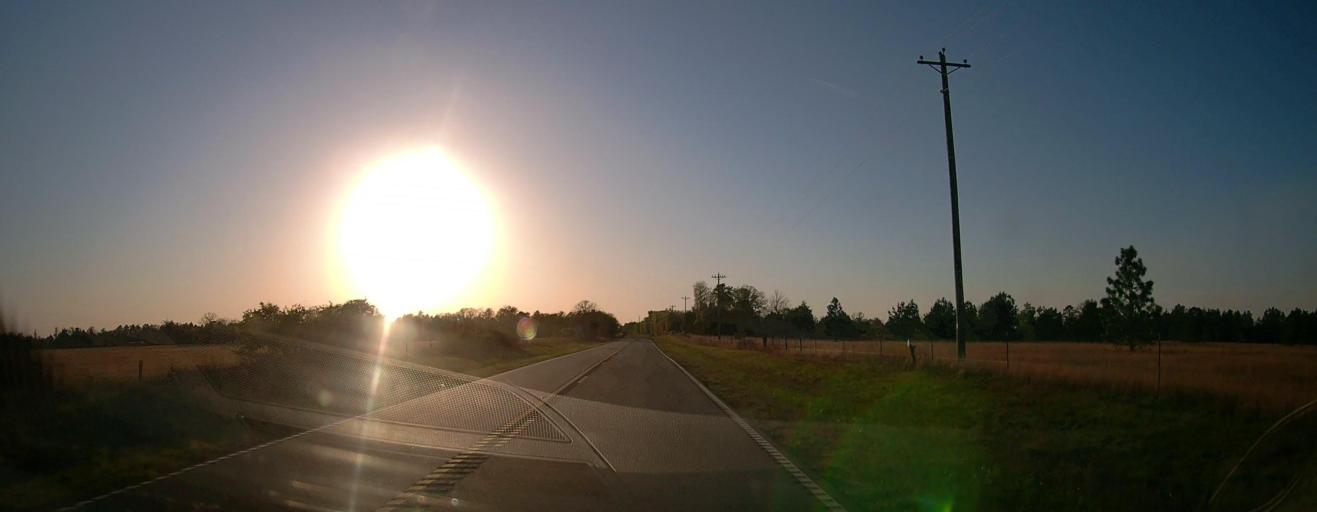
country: US
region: Georgia
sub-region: Talbot County
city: Talbotton
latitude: 32.5329
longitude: -84.4879
